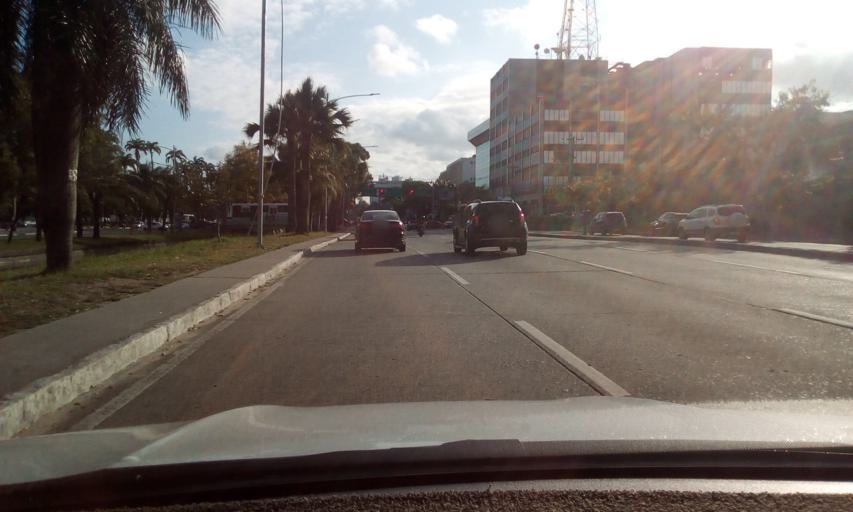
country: BR
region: Pernambuco
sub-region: Recife
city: Recife
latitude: -8.0504
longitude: -34.8945
